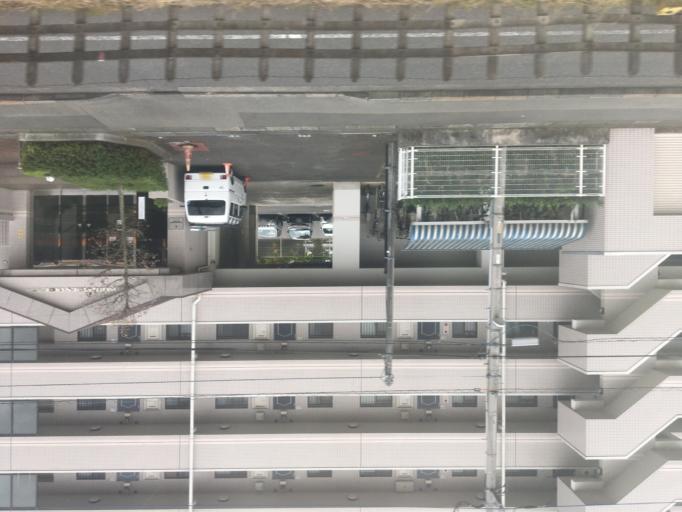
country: JP
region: Tokyo
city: Hino
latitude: 35.7054
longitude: 139.3873
